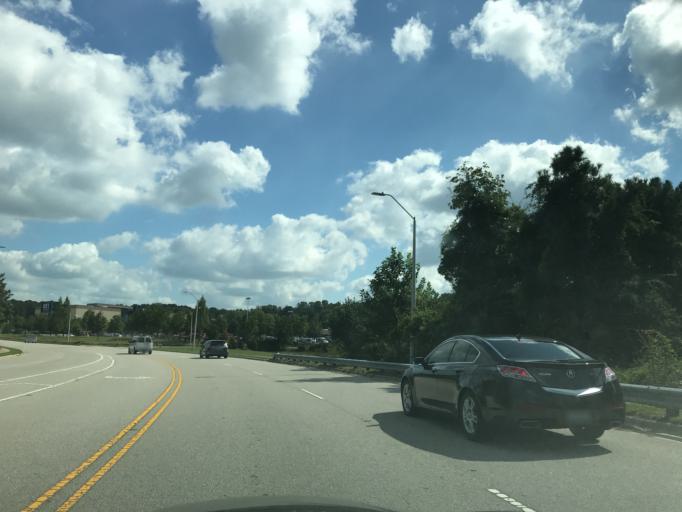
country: US
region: North Carolina
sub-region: Wake County
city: Raleigh
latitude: 35.8642
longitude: -78.5793
